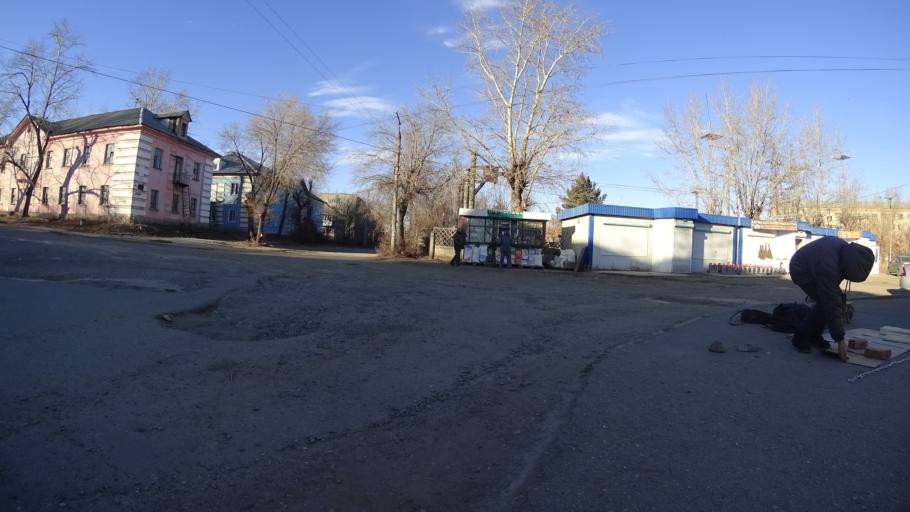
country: RU
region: Chelyabinsk
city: Troitsk
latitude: 54.0904
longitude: 61.5572
